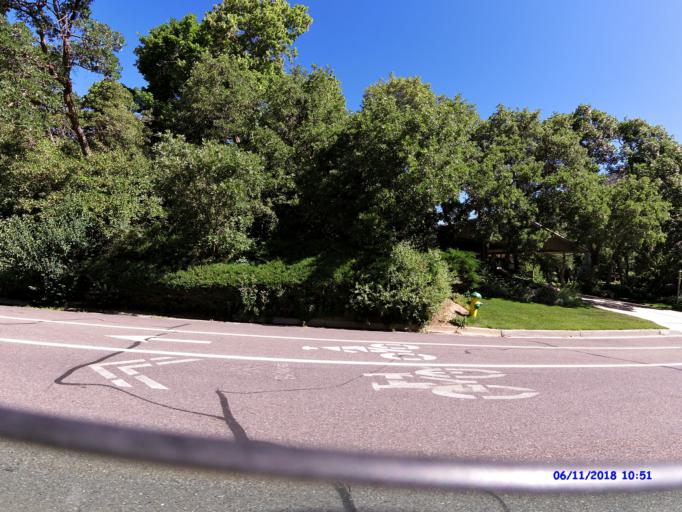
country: US
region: Utah
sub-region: Weber County
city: Ogden
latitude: 41.2117
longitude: -111.9345
